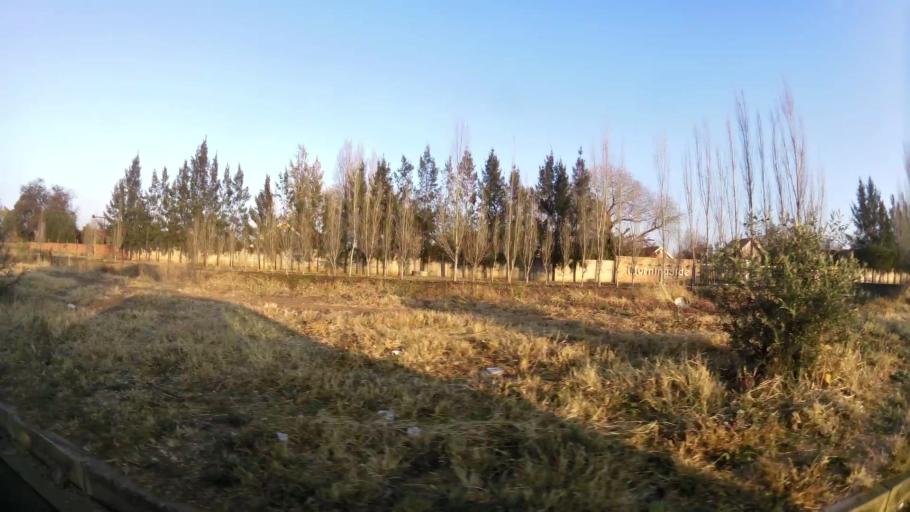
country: ZA
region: Orange Free State
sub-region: Mangaung Metropolitan Municipality
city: Bloemfontein
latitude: -29.1064
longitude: 26.1623
